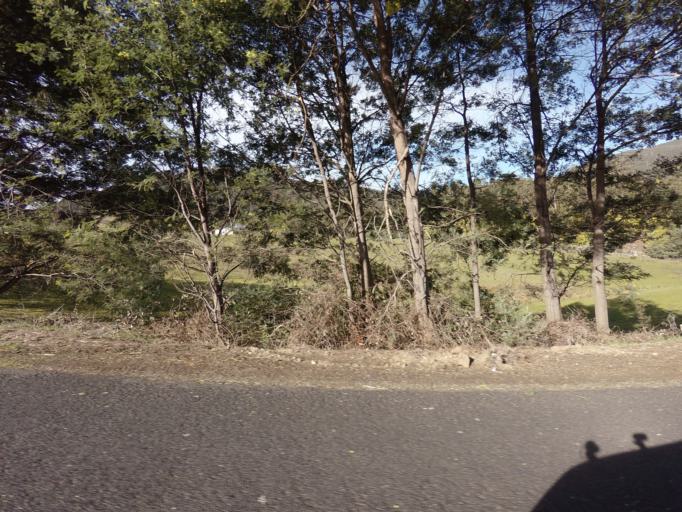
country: AU
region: Tasmania
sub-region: Kingborough
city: Kettering
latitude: -43.1708
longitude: 147.1682
